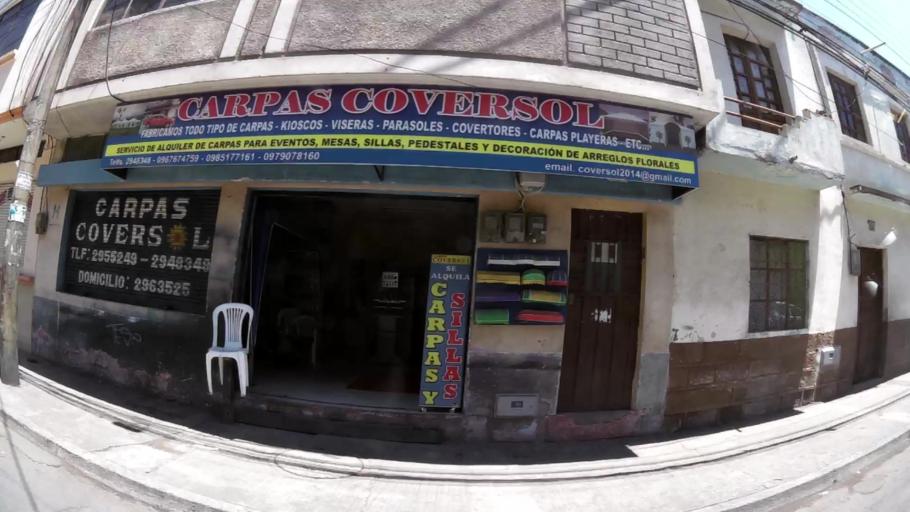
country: EC
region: Chimborazo
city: Riobamba
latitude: -1.6753
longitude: -78.6560
